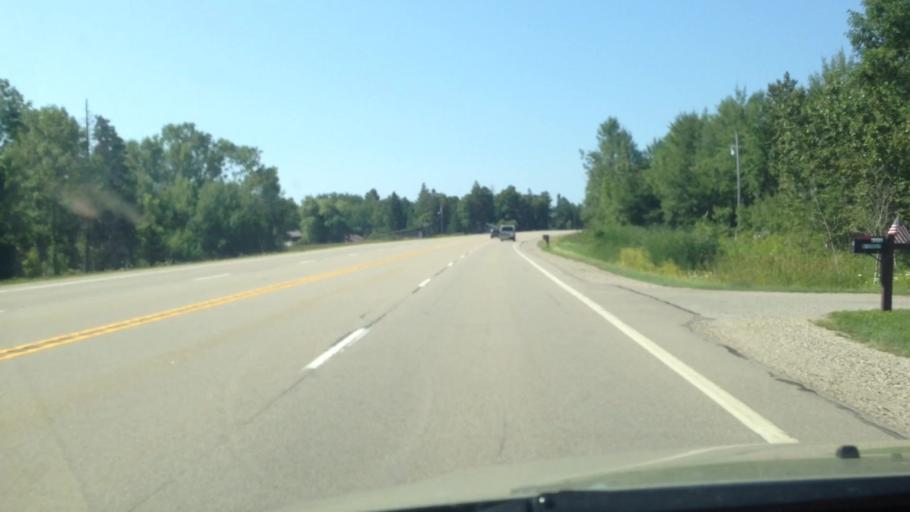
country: US
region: Michigan
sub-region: Delta County
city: Escanaba
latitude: 45.5486
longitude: -87.2709
